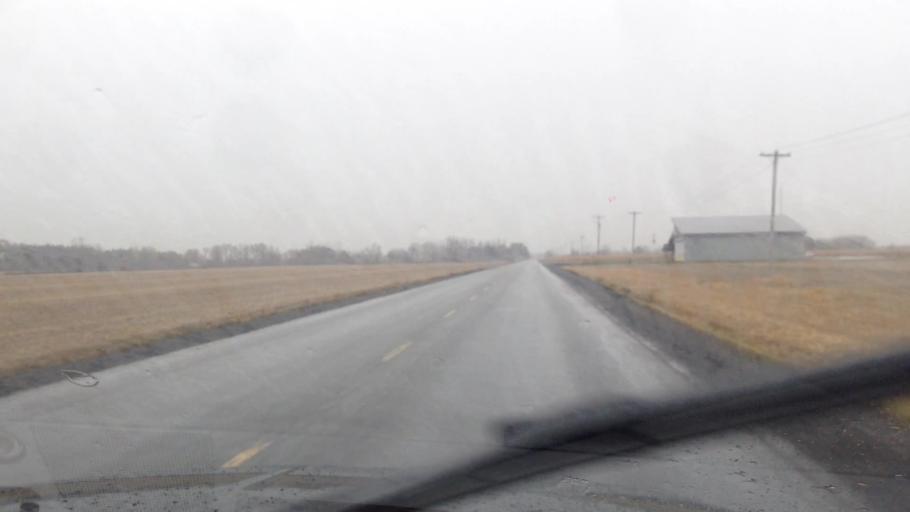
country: CA
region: Ontario
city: Bourget
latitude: 45.2829
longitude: -75.2925
